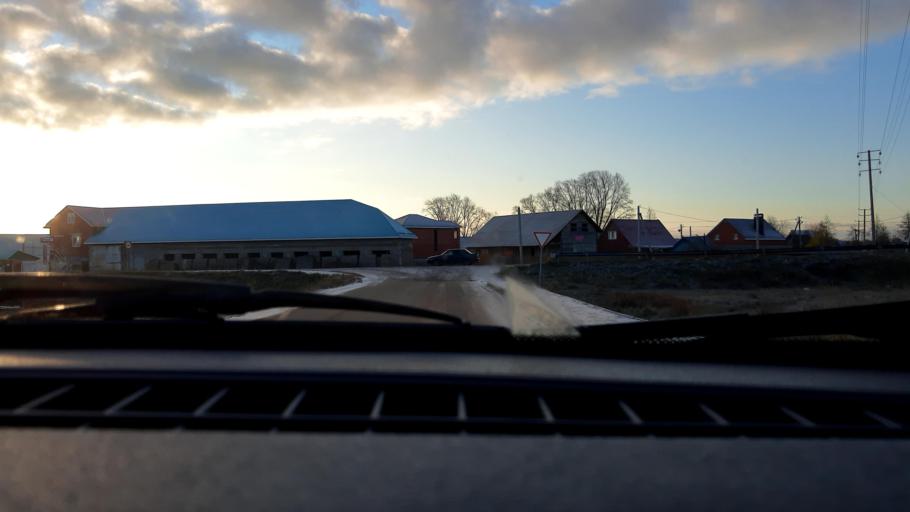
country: RU
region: Bashkortostan
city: Mikhaylovka
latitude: 54.7815
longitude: 55.8219
